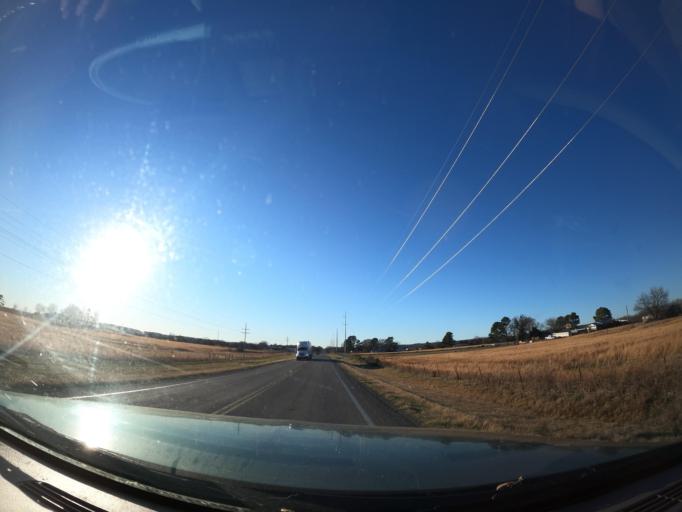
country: US
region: Oklahoma
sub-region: Latimer County
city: Wilburton
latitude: 34.9129
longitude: -95.4154
